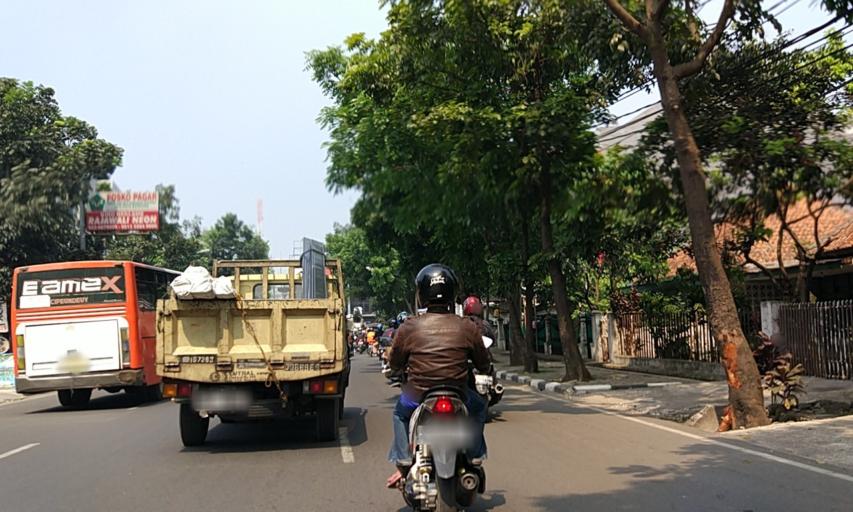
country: ID
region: West Java
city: Bandung
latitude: -6.9165
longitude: 107.5769
